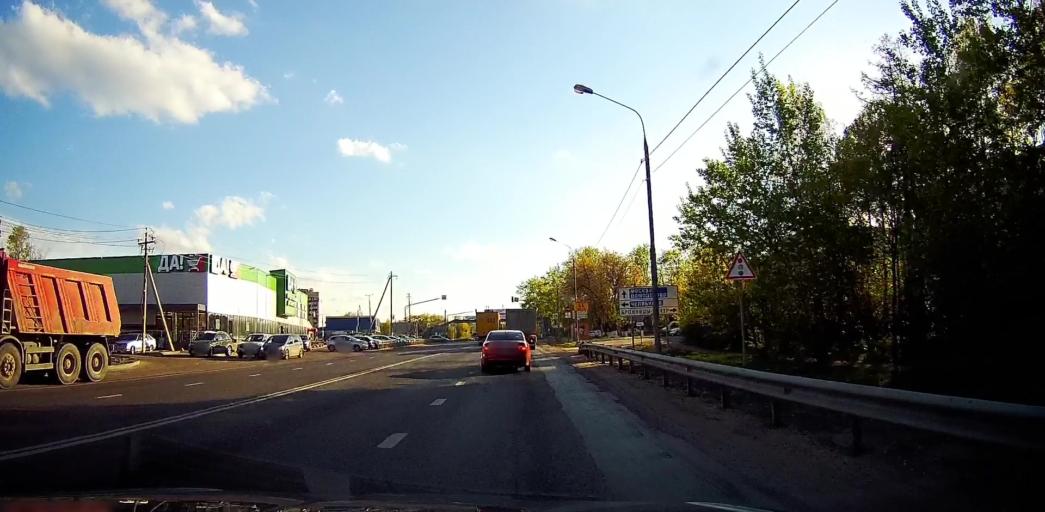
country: RU
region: Moskovskaya
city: Bronnitsy
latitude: 55.4166
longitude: 38.2845
